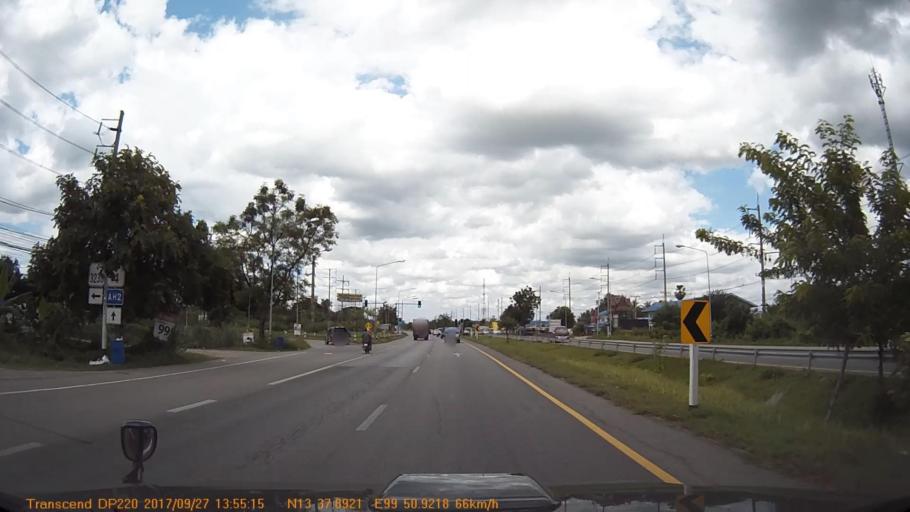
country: TH
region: Ratchaburi
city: Photharam
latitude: 13.6317
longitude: 99.8488
